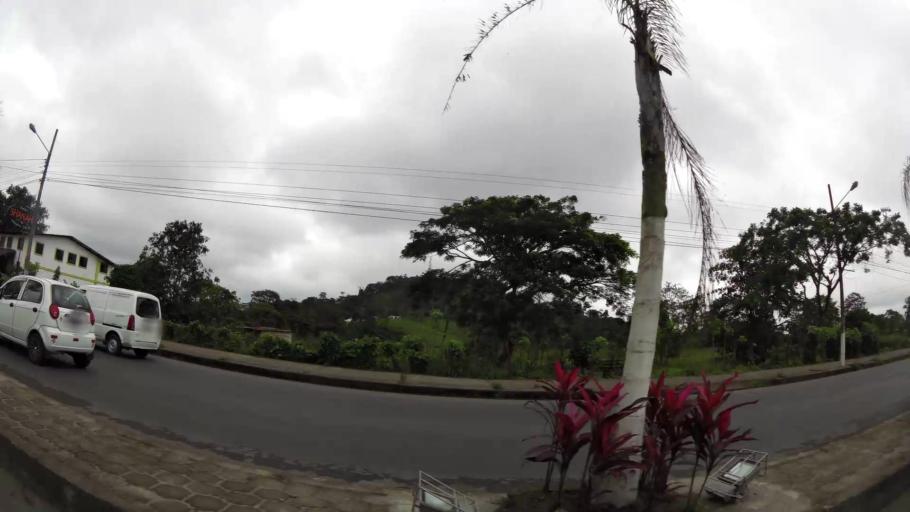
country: EC
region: Santo Domingo de los Tsachilas
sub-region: Canton Santo Domingo de los Colorados
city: Santo Domingo de los Colorados
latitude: -0.2549
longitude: -79.1930
